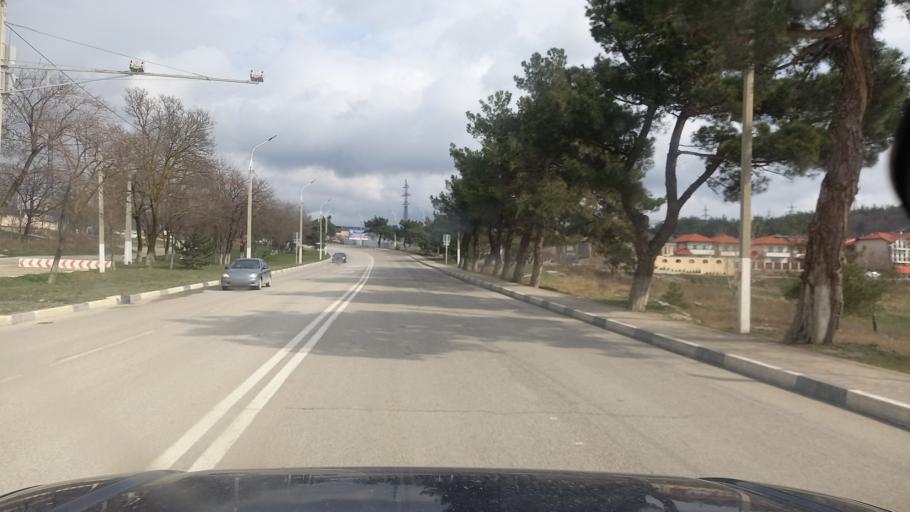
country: RU
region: Krasnodarskiy
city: Gelendzhik
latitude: 44.5540
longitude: 38.1156
